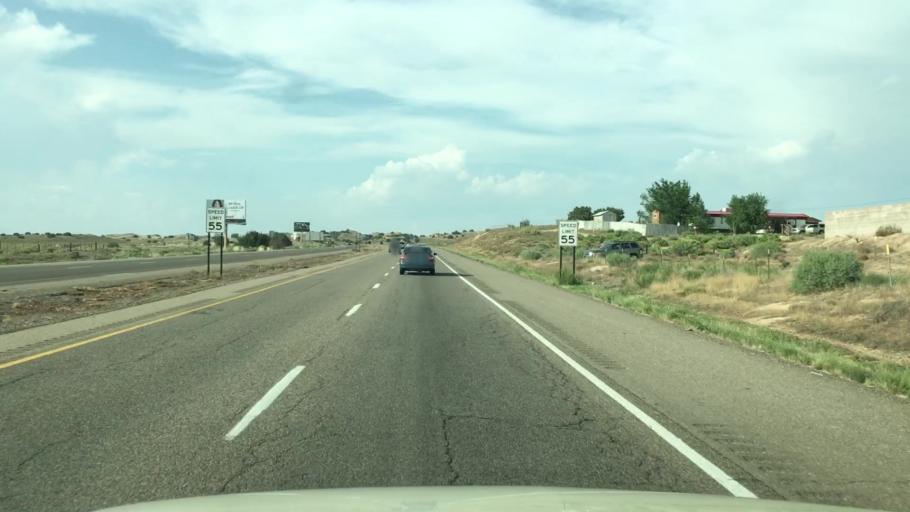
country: US
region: New Mexico
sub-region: Santa Fe County
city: Pojoaque
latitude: 35.9106
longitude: -106.0173
